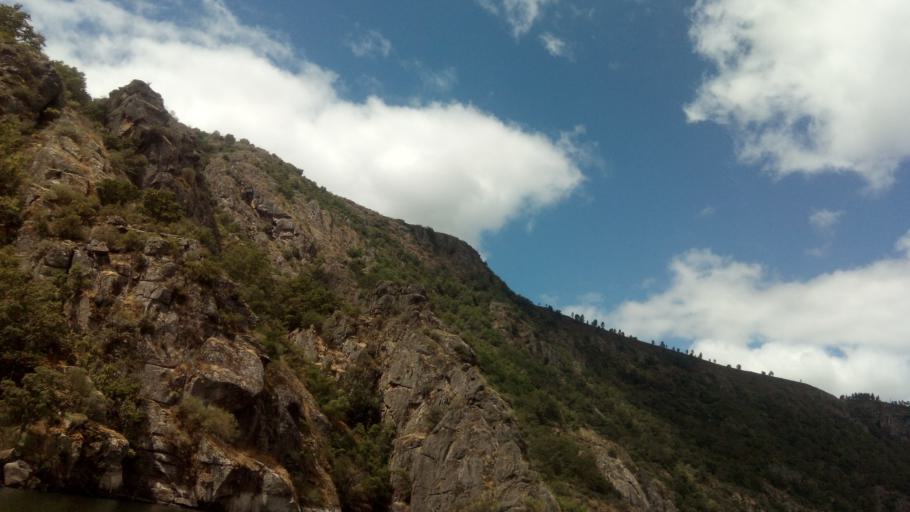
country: ES
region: Galicia
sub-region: Provincia de Lugo
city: Sober
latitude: 42.3916
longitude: -7.6224
